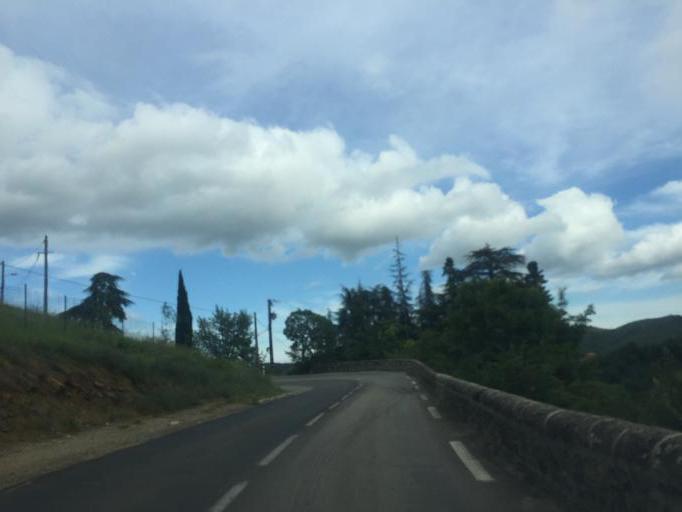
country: FR
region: Rhone-Alpes
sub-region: Departement de l'Ardeche
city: Privas
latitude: 44.7413
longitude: 4.6042
